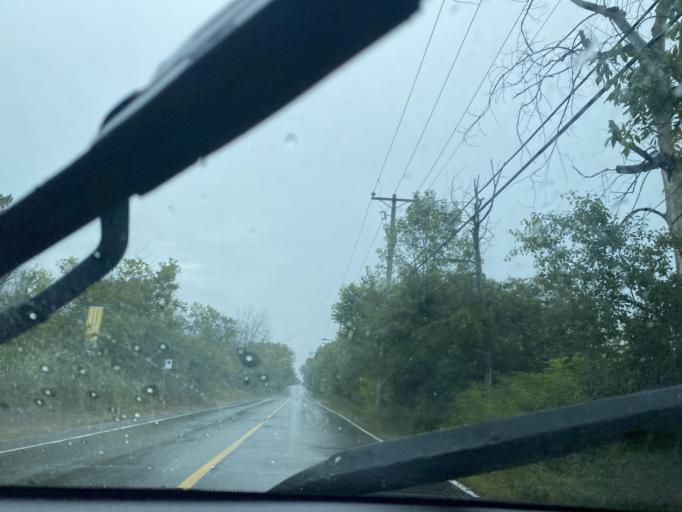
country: CA
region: Quebec
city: Baie-D'Urfe
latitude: 45.4581
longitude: -73.9277
